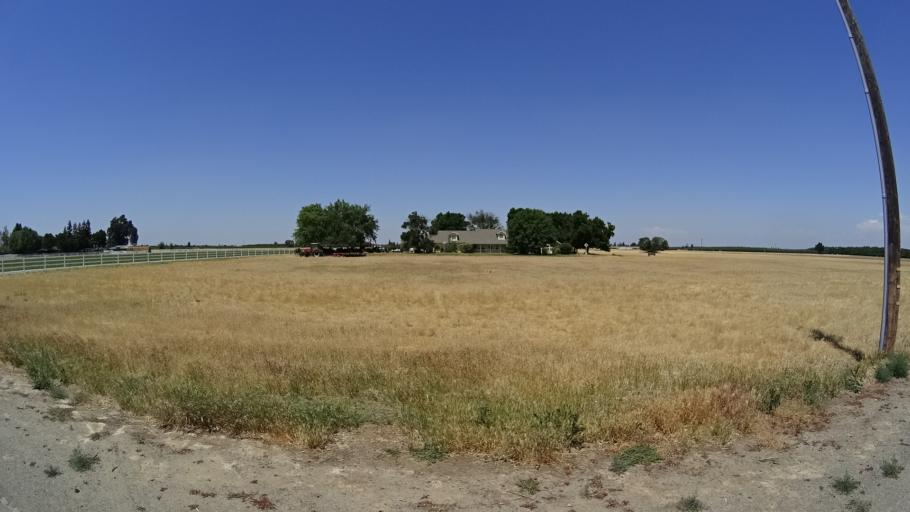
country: US
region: California
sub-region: Kings County
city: Lucerne
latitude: 36.3864
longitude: -119.6252
